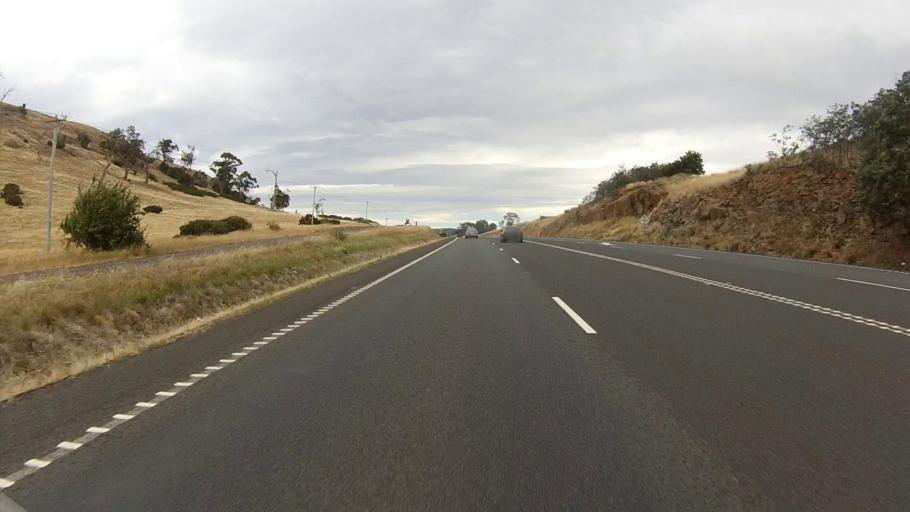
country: AU
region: Tasmania
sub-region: Brighton
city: Bridgewater
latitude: -42.3371
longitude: 147.3425
